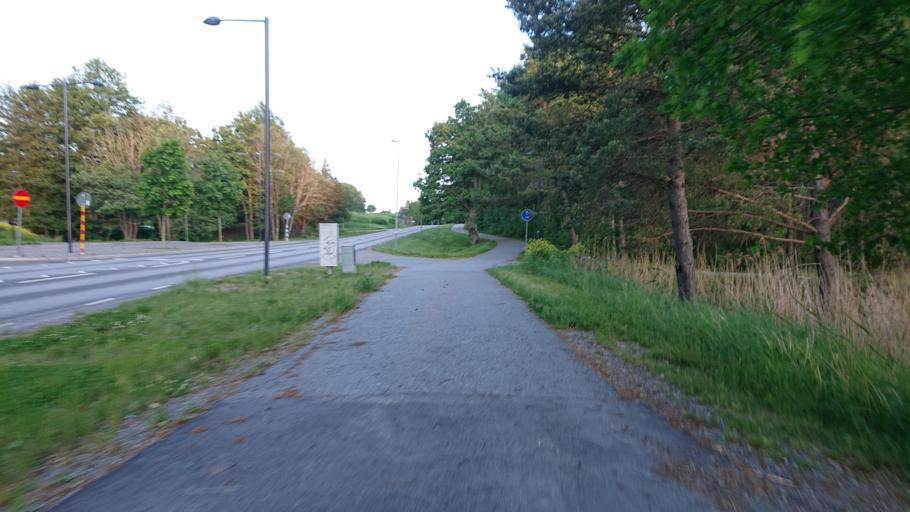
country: SE
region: Stockholm
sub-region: Osterakers Kommun
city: Akersberga
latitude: 59.4999
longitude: 18.3151
